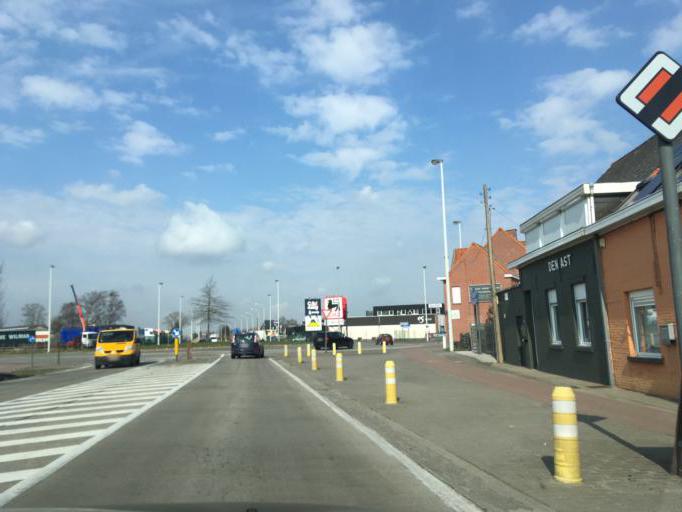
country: BE
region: Flanders
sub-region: Provincie West-Vlaanderen
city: Izegem
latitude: 50.9030
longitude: 3.2221
